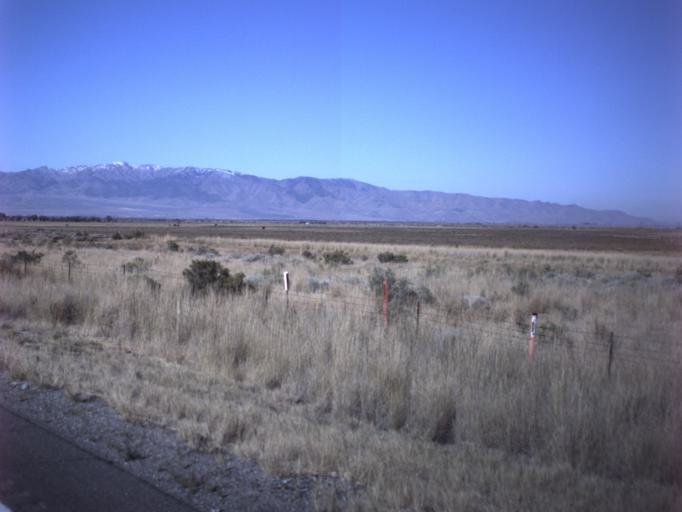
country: US
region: Utah
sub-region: Tooele County
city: Erda
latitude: 40.6349
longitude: -112.3310
